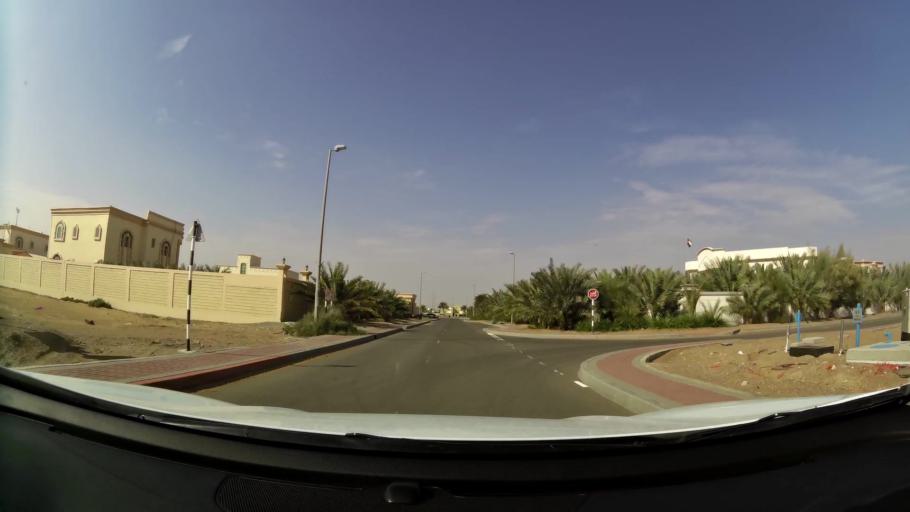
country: AE
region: Abu Dhabi
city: Al Ain
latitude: 24.0909
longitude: 55.8997
